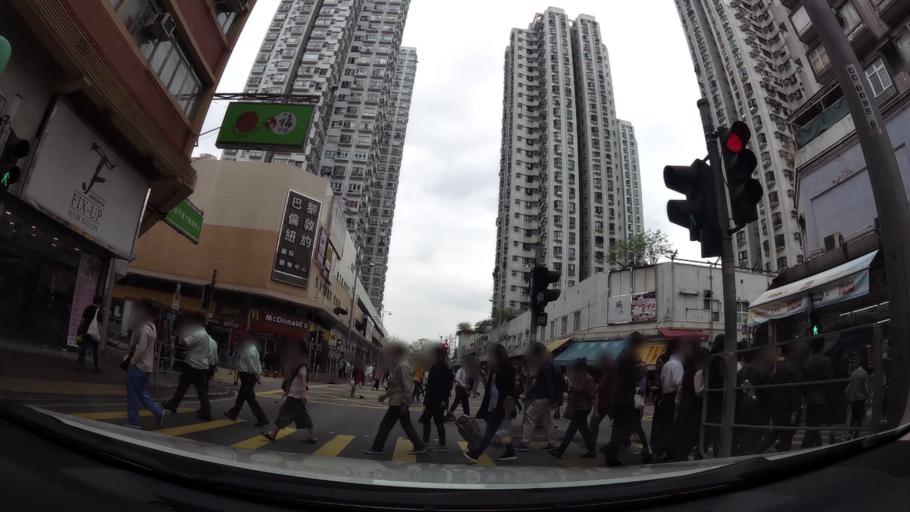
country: HK
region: Tuen Mun
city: Tuen Mun
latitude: 22.3977
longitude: 113.9749
